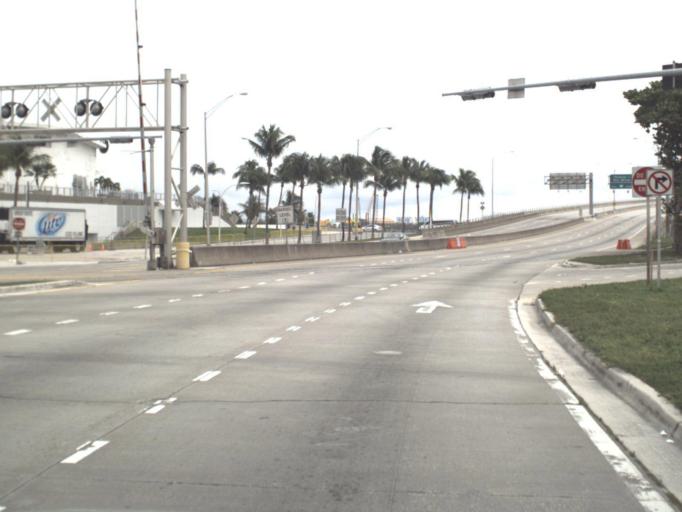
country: US
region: Florida
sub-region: Miami-Dade County
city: Miami
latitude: 25.7800
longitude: -80.1878
